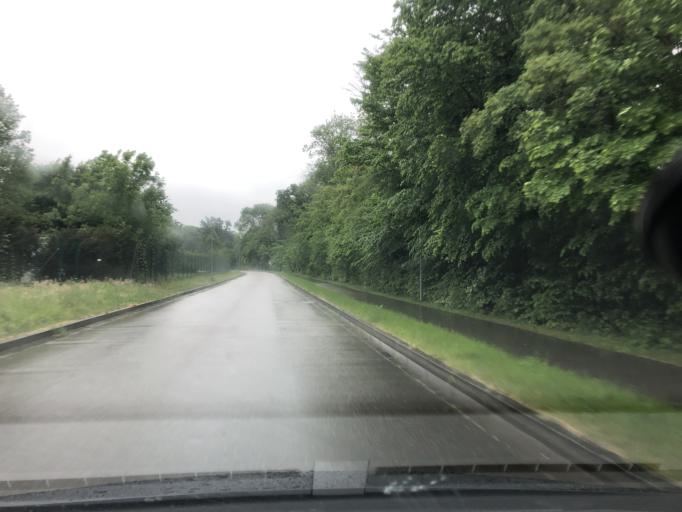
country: DE
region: Baden-Wuerttemberg
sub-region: Karlsruhe Region
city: Kronau
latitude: 49.2405
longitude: 8.6469
